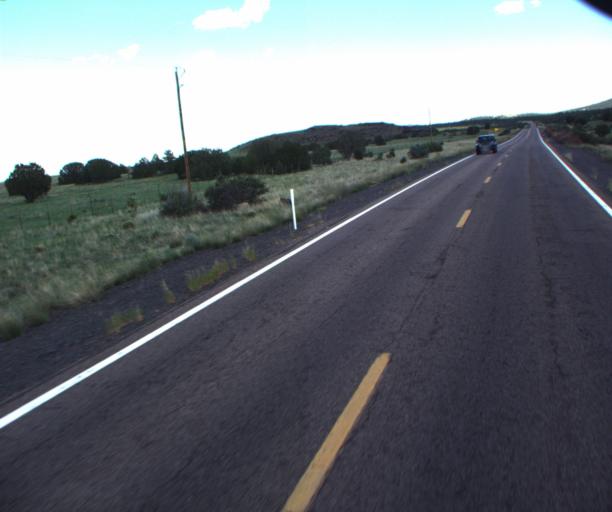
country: US
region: Arizona
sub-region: Navajo County
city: Pinetop-Lakeside
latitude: 34.2699
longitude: -109.6345
